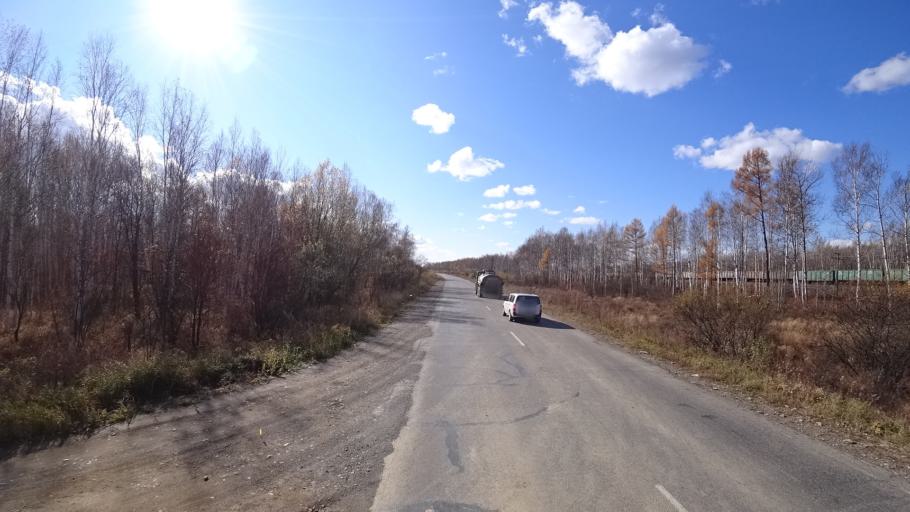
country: RU
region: Khabarovsk Krai
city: Amursk
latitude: 50.1121
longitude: 136.5206
